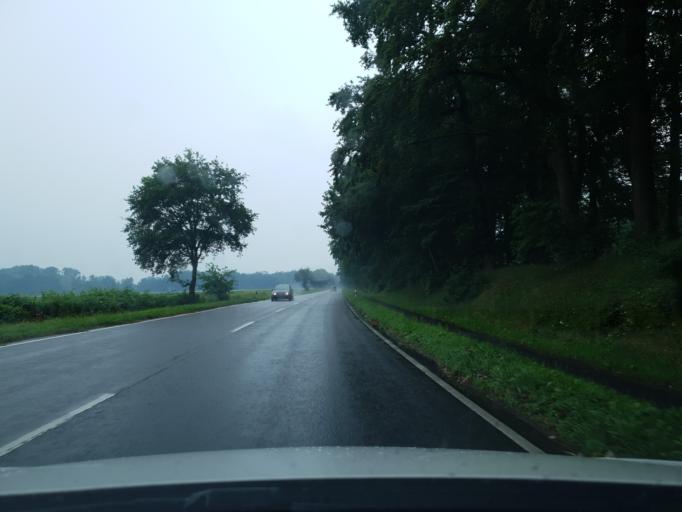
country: DE
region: Lower Saxony
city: Lingen
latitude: 52.5422
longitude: 7.2936
